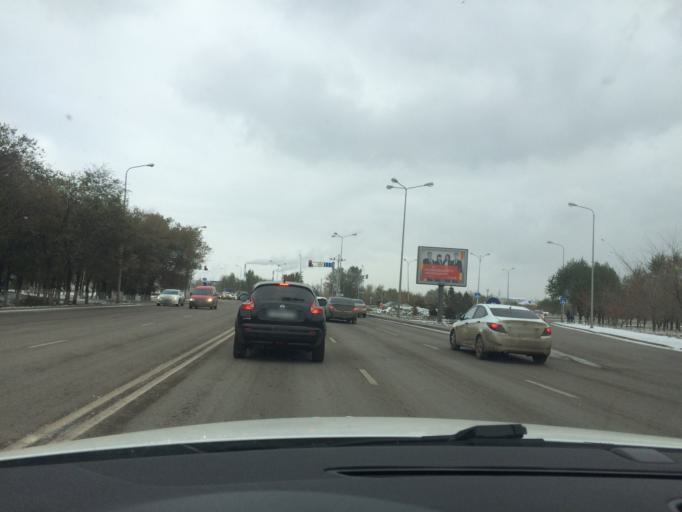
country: KZ
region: Astana Qalasy
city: Astana
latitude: 51.1646
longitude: 71.4740
